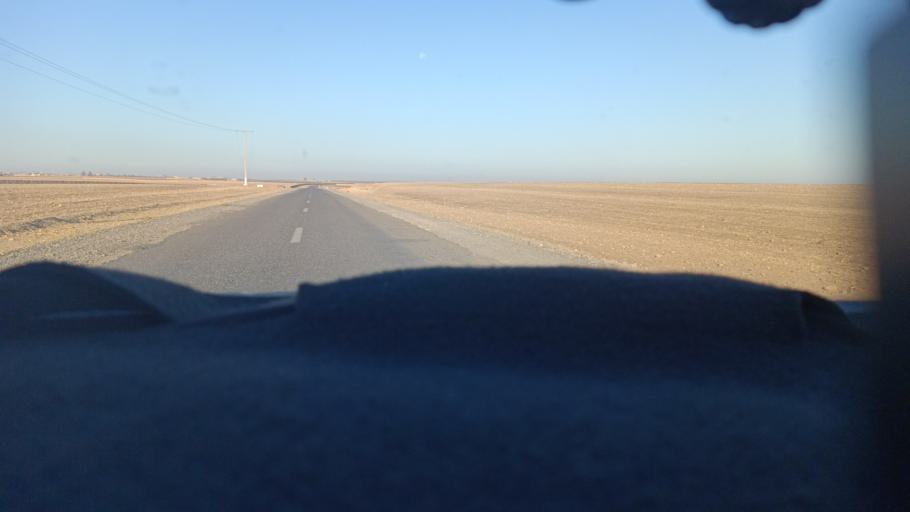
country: MA
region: Doukkala-Abda
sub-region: Safi
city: Youssoufia
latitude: 32.3713
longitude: -8.6866
